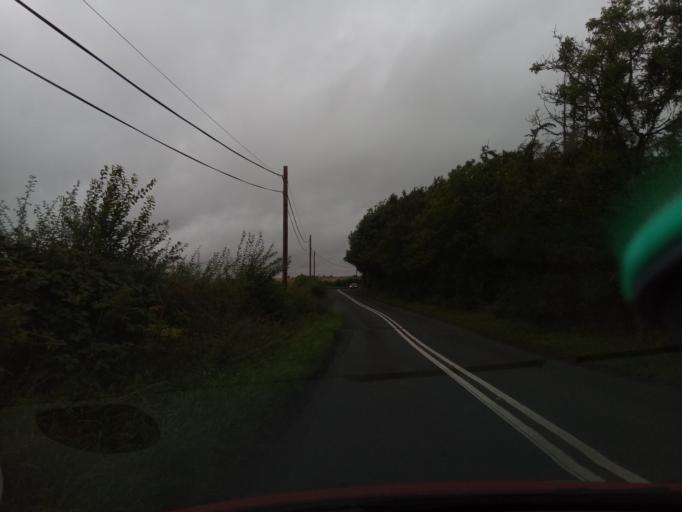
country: GB
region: Scotland
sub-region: The Scottish Borders
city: Kelso
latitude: 55.6220
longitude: -2.4882
